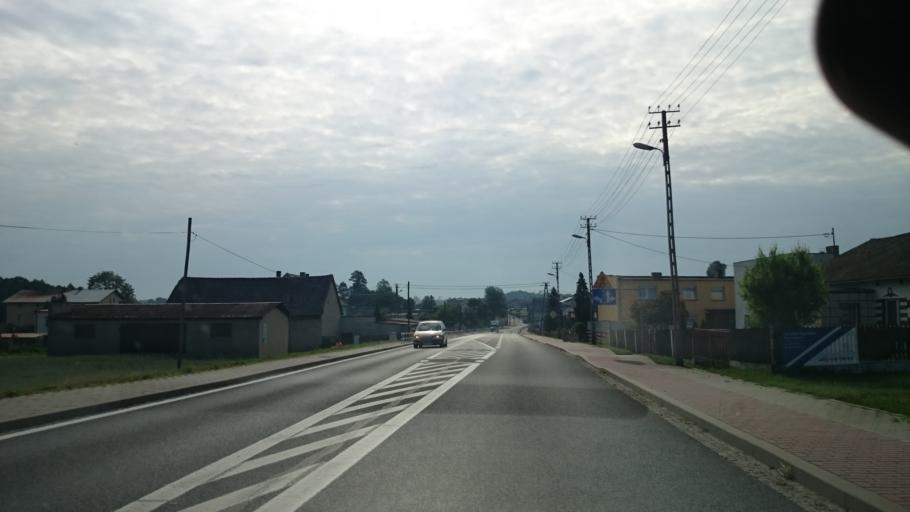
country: PL
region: Opole Voivodeship
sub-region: Powiat strzelecki
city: Jemielnica
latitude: 50.4896
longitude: 18.4065
